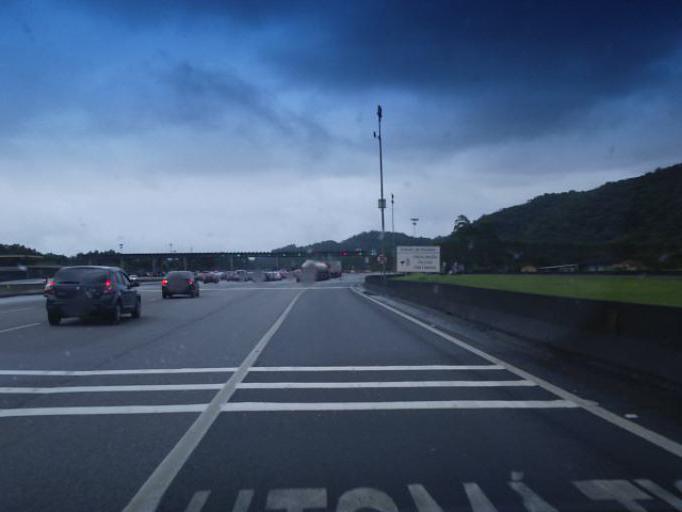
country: BR
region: Santa Catarina
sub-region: Barra Velha
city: Barra Velha
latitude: -26.5935
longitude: -48.7220
